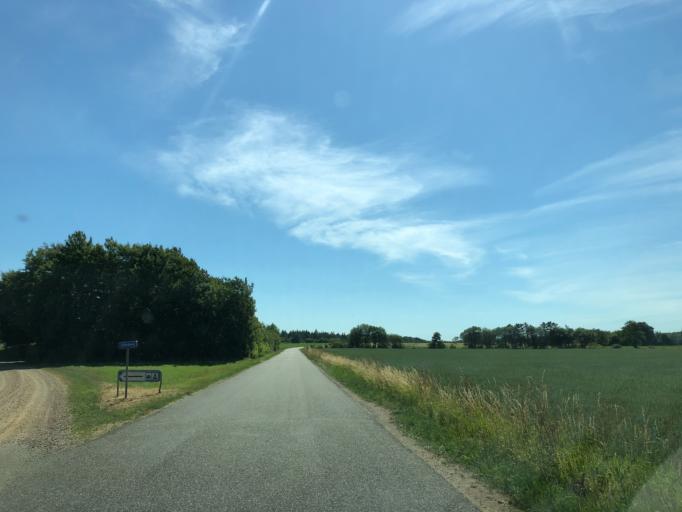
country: DK
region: Central Jutland
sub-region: Skive Kommune
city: Skive
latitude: 56.4459
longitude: 8.9730
